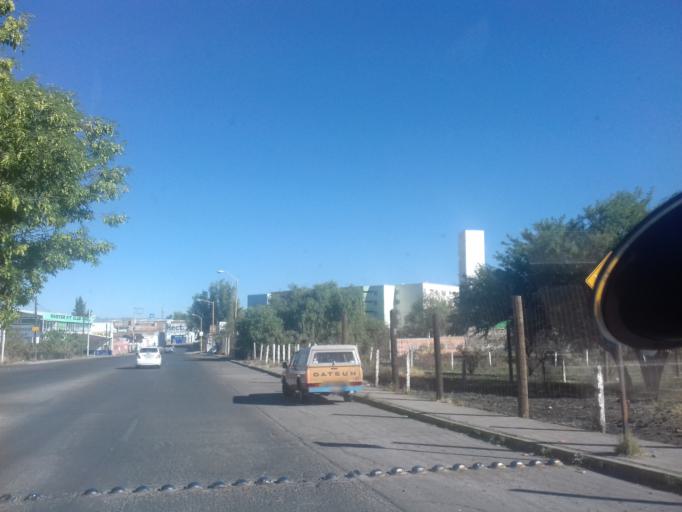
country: MX
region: Aguascalientes
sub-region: Aguascalientes
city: Aguascalientes
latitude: 21.8642
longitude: -102.2751
